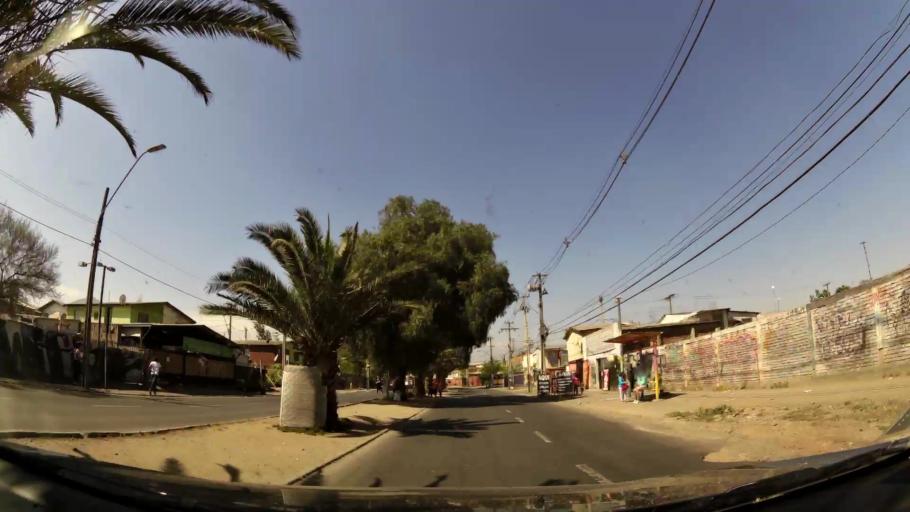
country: CL
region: Santiago Metropolitan
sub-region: Provincia de Santiago
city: Lo Prado
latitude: -33.4071
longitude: -70.7391
